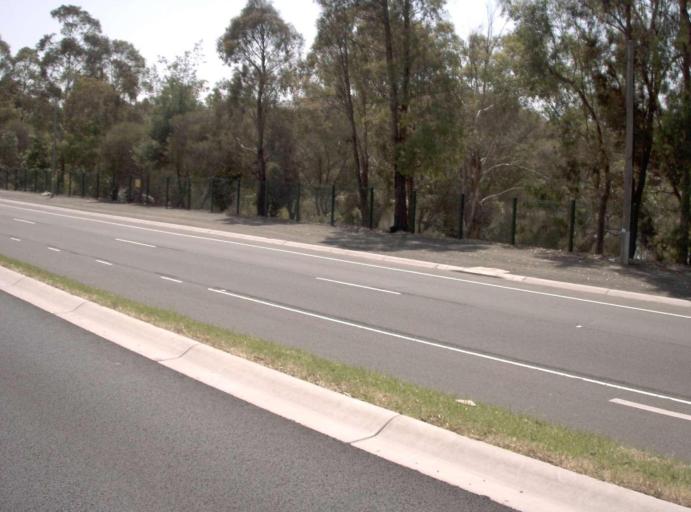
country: AU
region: Victoria
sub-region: Manningham
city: Bulleen
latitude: -37.7722
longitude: 145.0790
